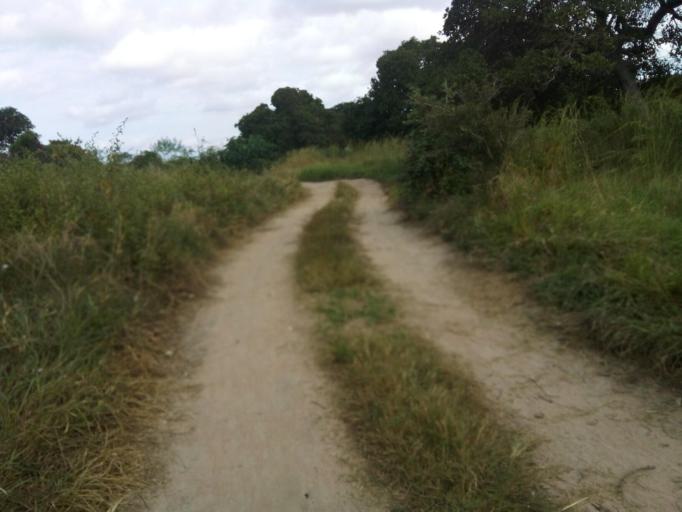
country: MZ
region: Zambezia
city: Quelimane
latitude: -17.5542
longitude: 36.6992
